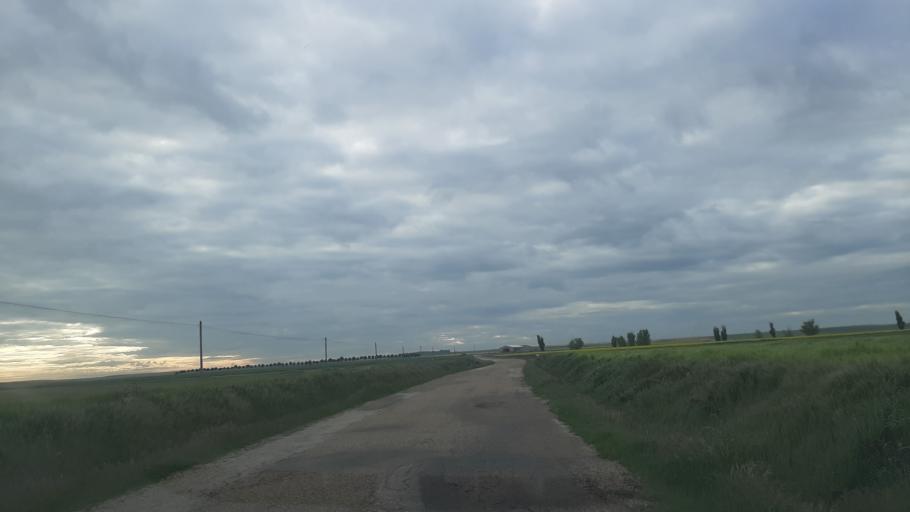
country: ES
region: Castille and Leon
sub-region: Provincia de Salamanca
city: Villaflores
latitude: 41.0823
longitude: -5.2257
